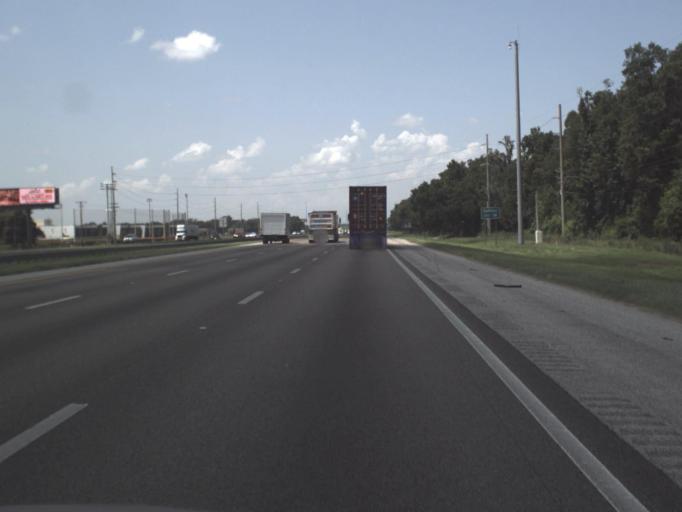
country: US
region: Florida
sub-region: Hillsborough County
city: Dover
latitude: 28.0261
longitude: -82.2301
